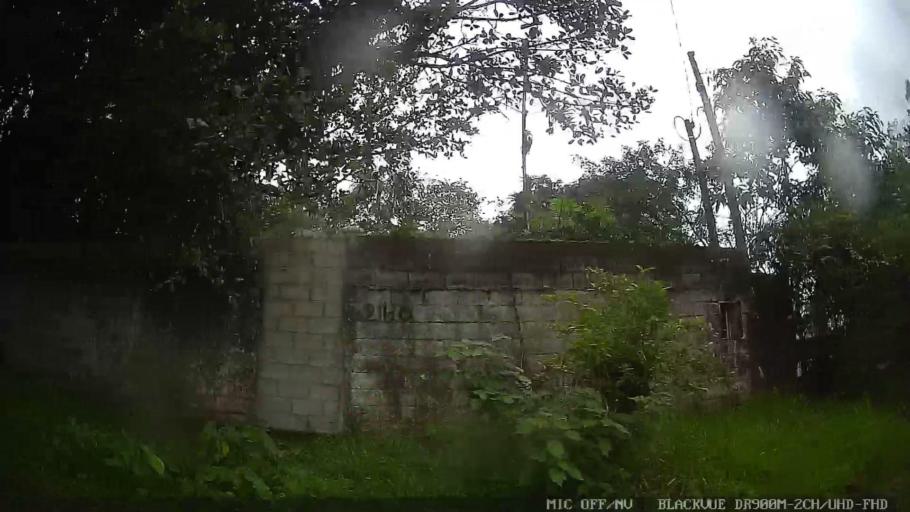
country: BR
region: Sao Paulo
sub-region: Itanhaem
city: Itanhaem
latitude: -24.1739
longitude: -46.8261
